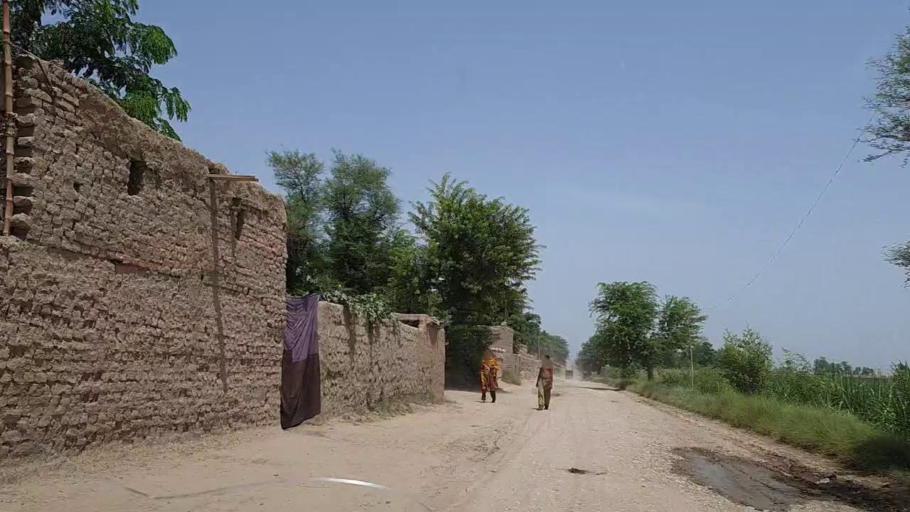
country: PK
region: Sindh
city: Tharu Shah
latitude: 26.9032
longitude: 68.0066
